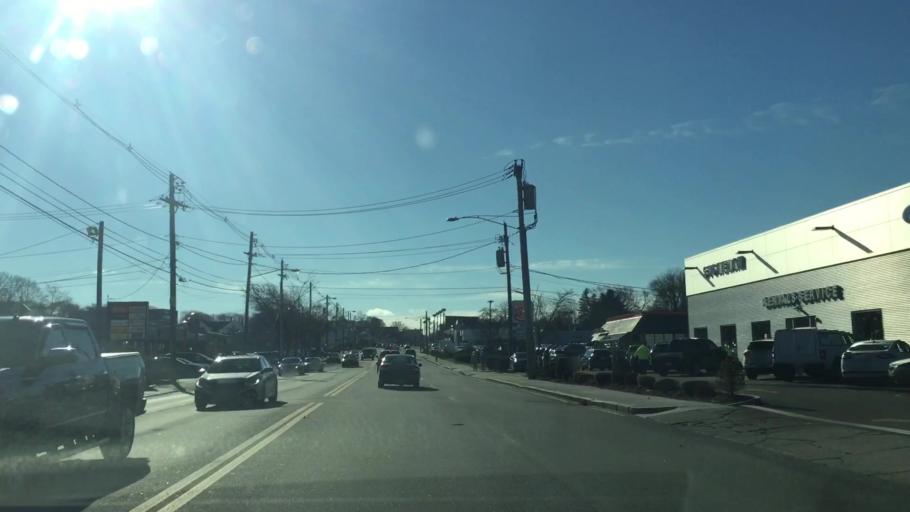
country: US
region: Massachusetts
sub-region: Middlesex County
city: Stoneham
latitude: 42.4896
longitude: -71.1003
